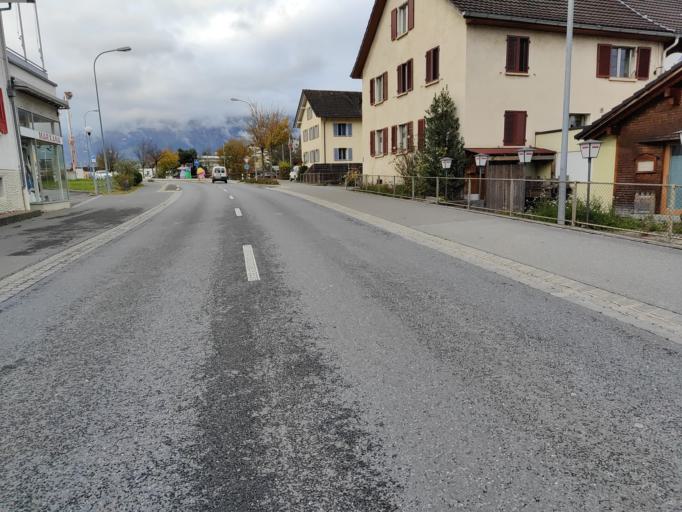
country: LI
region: Eschen
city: Eschen
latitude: 47.2093
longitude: 9.5230
